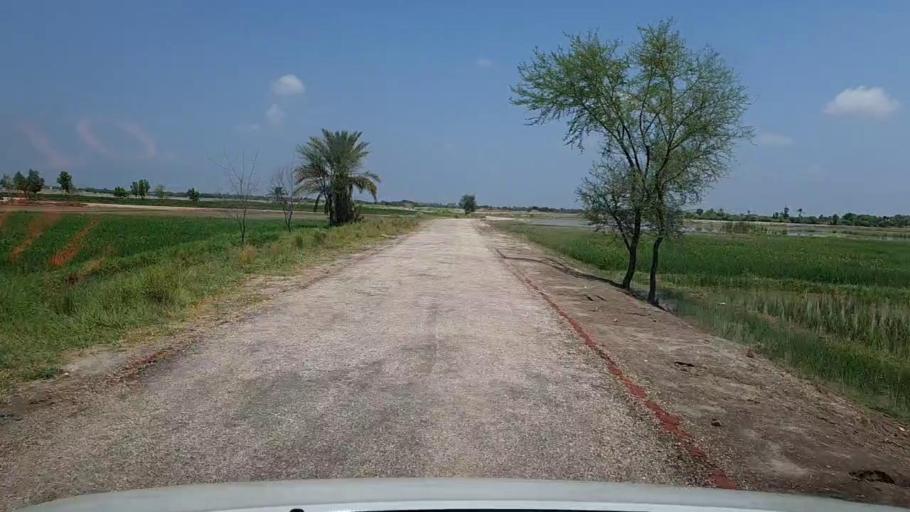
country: PK
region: Sindh
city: Kandiaro
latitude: 26.9849
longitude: 68.2186
